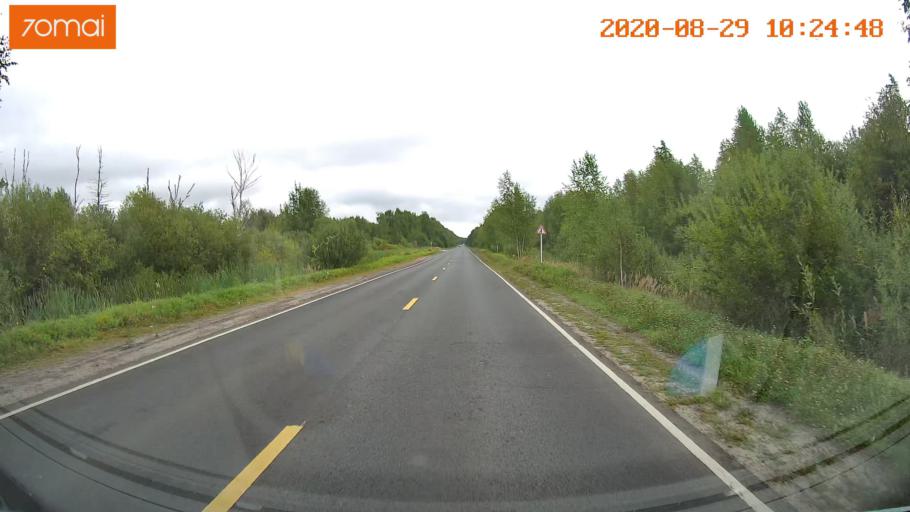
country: RU
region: Ivanovo
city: Yur'yevets
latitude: 57.3202
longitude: 43.0066
